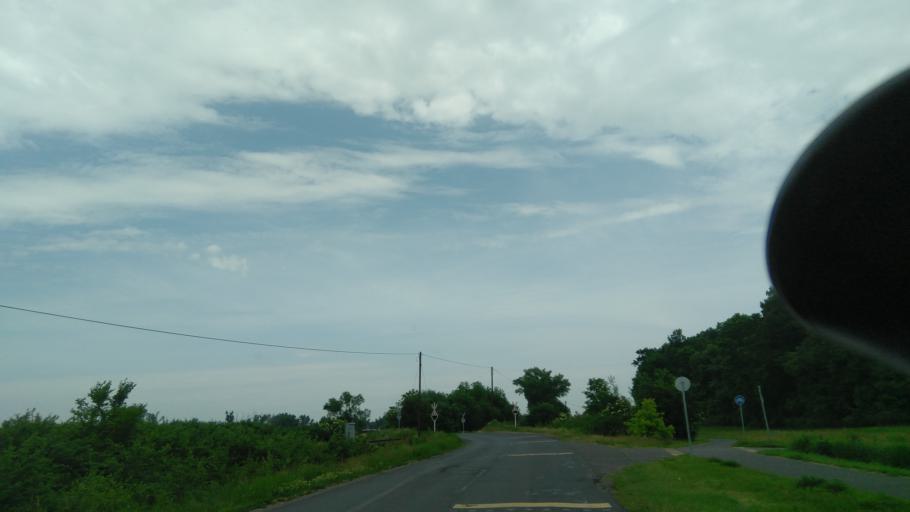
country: HU
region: Bekes
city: Fuzesgyarmat
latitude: 47.0780
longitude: 21.1951
